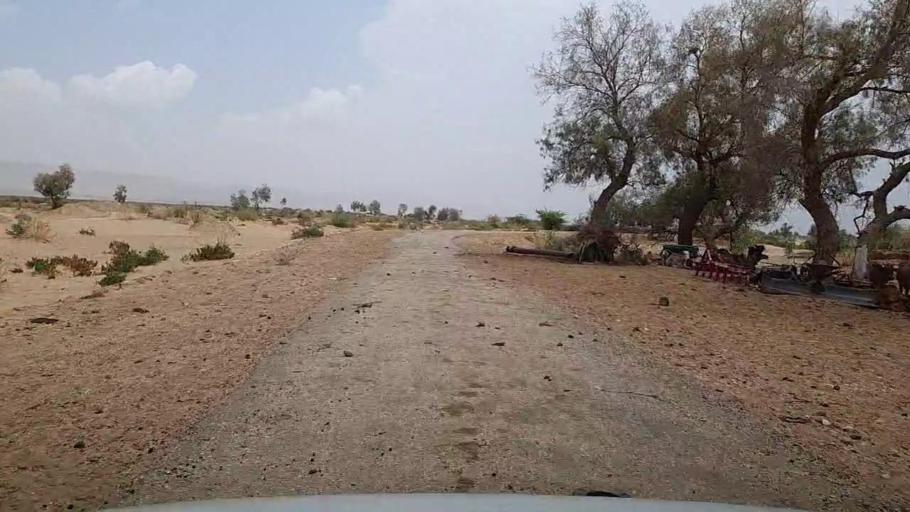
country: PK
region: Sindh
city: Sehwan
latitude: 26.3468
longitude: 67.7949
